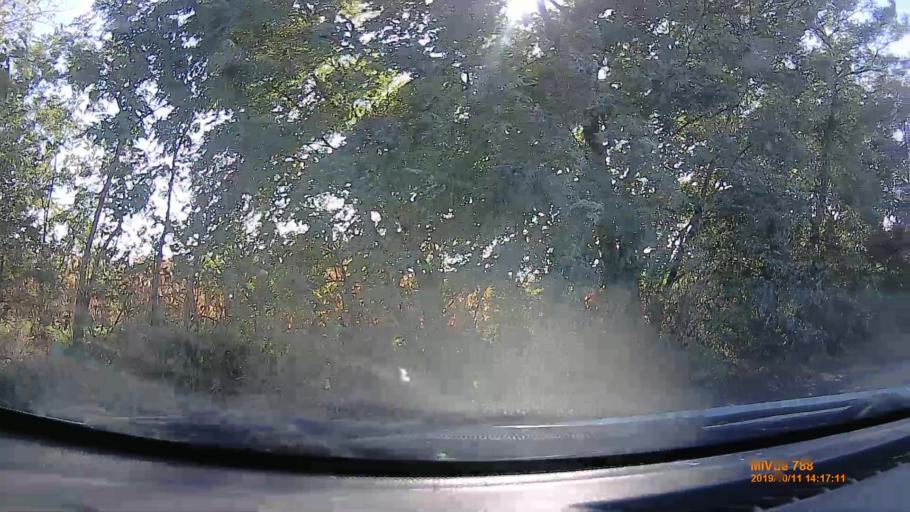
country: HU
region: Hajdu-Bihar
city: Hajduszoboszlo
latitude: 47.5298
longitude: 21.4017
